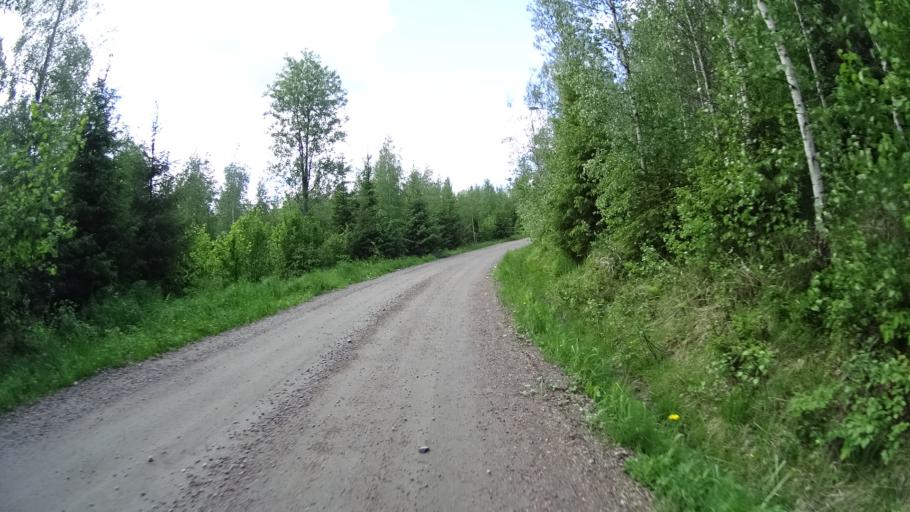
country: FI
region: Uusimaa
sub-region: Raaseporin
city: Karis
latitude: 60.1589
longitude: 23.6109
